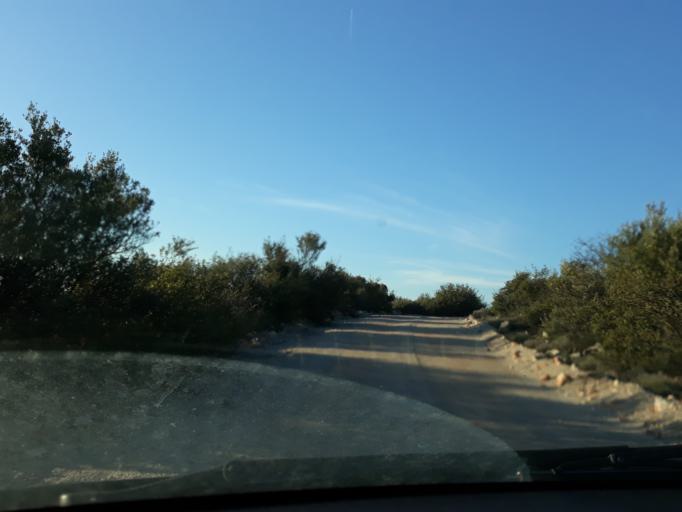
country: GR
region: Central Greece
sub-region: Nomos Voiotias
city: Asopia
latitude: 38.2671
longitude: 23.5312
